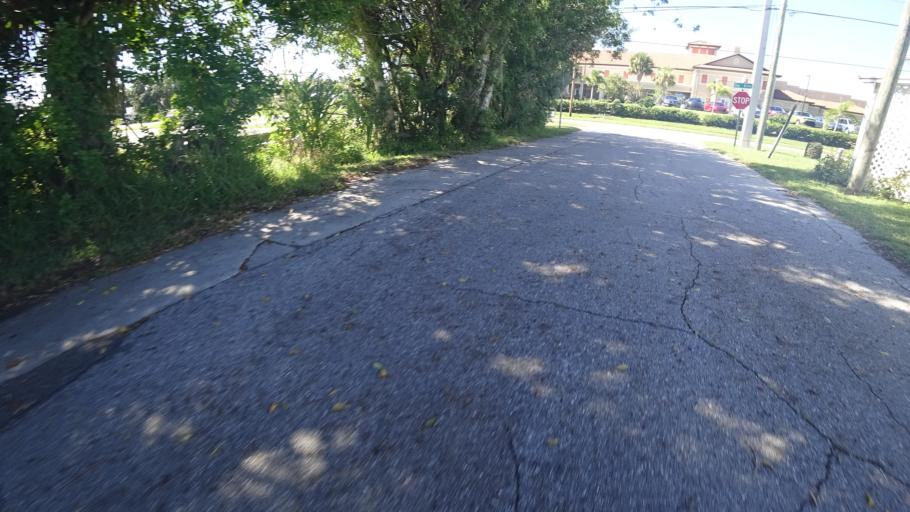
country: US
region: Florida
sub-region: Manatee County
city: Whitfield
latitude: 27.4186
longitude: -82.5775
